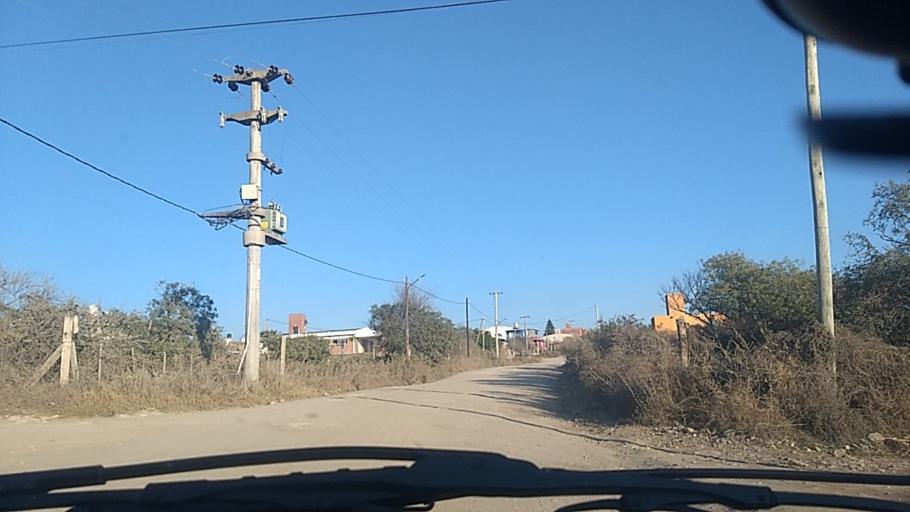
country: AR
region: Cordoba
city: Salsipuedes
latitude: -31.1412
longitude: -64.2832
